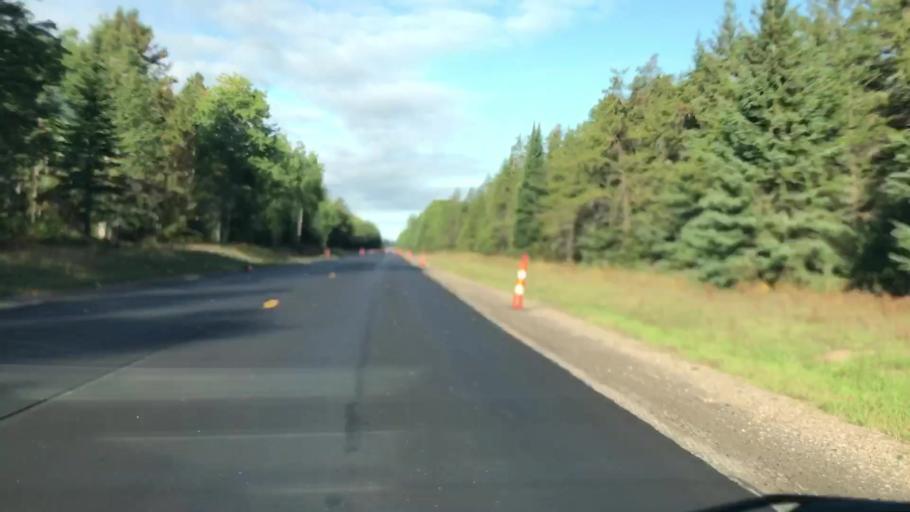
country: US
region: Michigan
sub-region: Mackinac County
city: Saint Ignace
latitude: 46.3459
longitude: -84.9265
